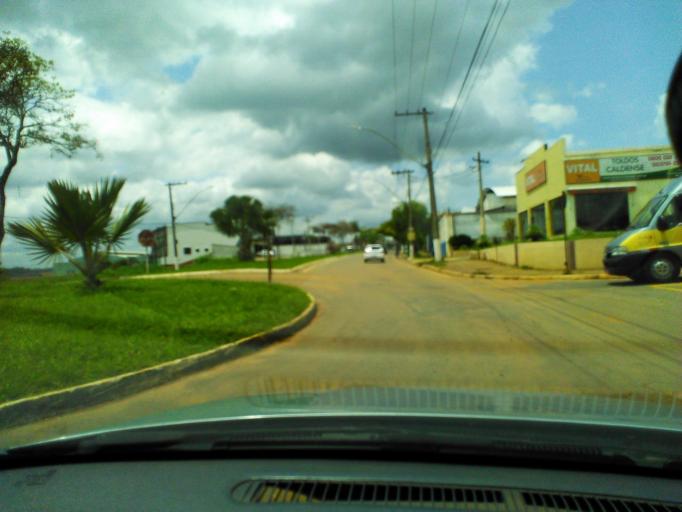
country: BR
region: Minas Gerais
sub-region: Tres Coracoes
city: Tres Coracoes
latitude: -21.6773
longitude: -45.2688
